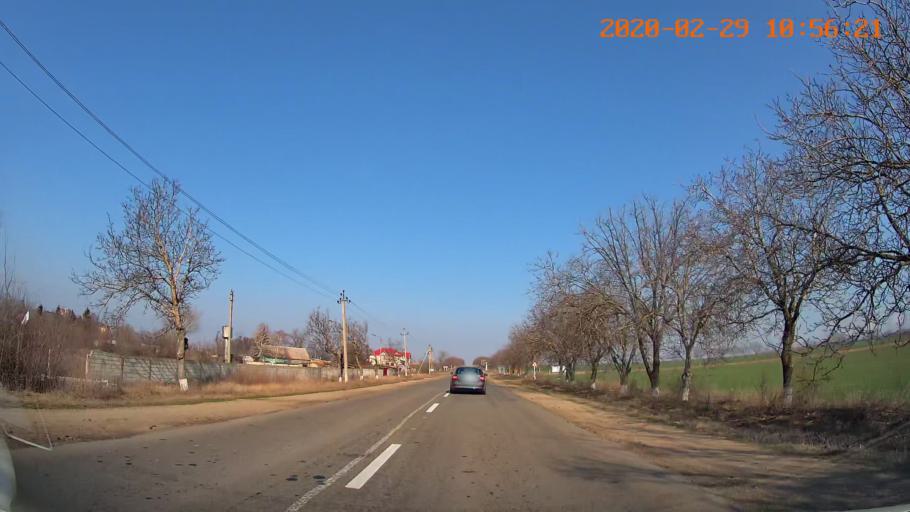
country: MD
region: Telenesti
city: Grigoriopol
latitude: 47.1447
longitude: 29.3247
